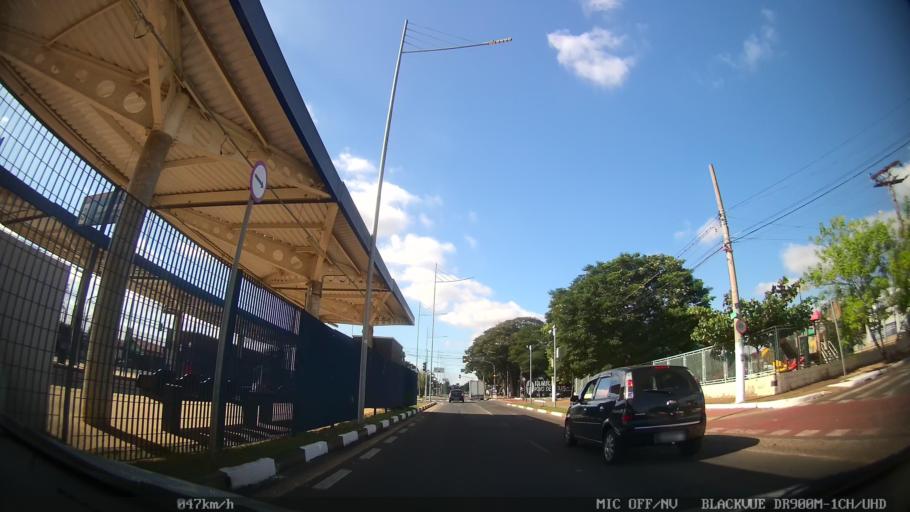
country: BR
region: Sao Paulo
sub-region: Hortolandia
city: Hortolandia
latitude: -22.8753
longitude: -47.2061
